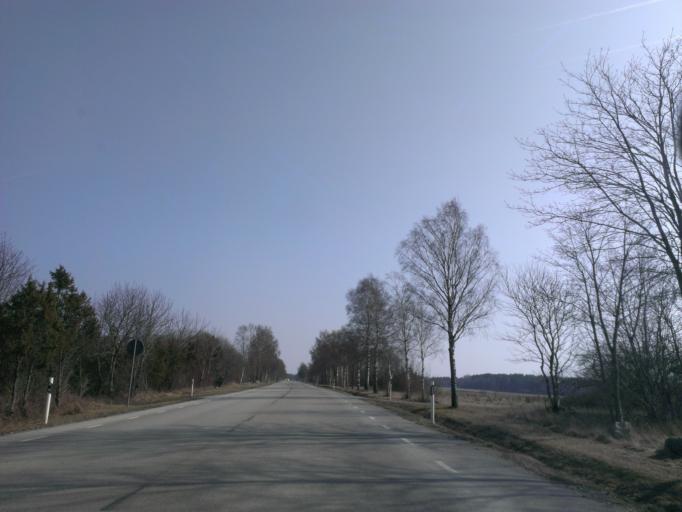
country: EE
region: Saare
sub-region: Orissaare vald
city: Orissaare
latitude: 58.5561
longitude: 23.0966
